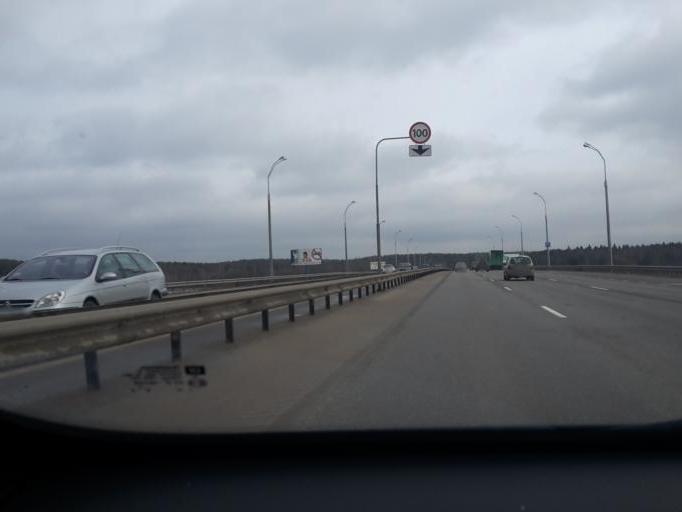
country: BY
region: Minsk
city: Zhdanovichy
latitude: 53.9563
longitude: 27.4528
